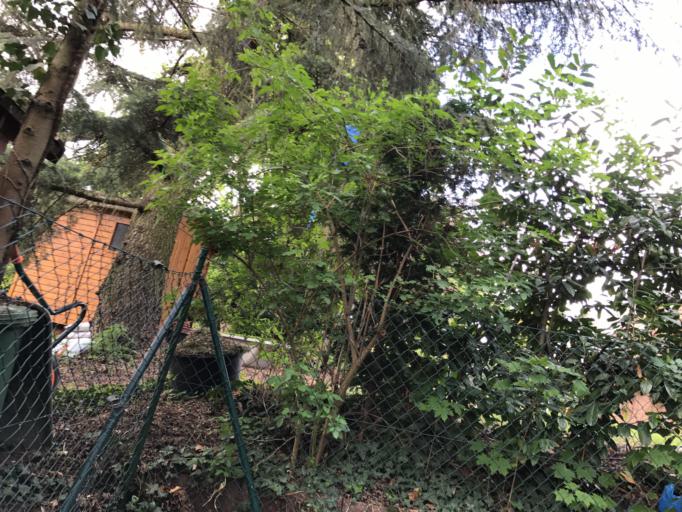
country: DE
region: Rheinland-Pfalz
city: Mainz
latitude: 49.9839
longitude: 8.2609
